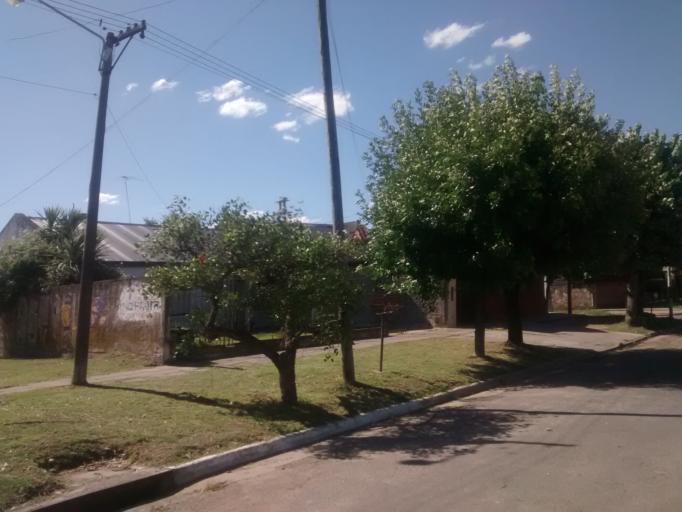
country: AR
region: Buenos Aires
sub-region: Partido de La Plata
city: La Plata
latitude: -34.9347
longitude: -57.9013
